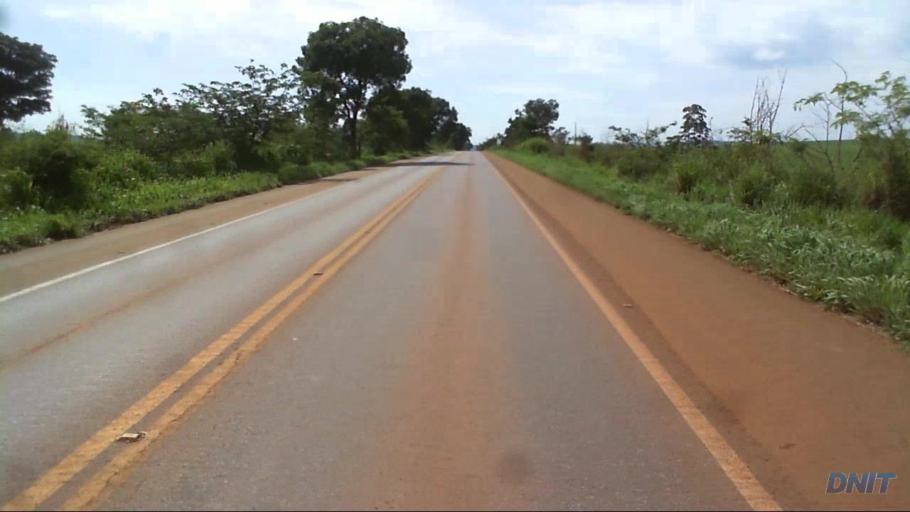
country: BR
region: Goias
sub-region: Barro Alto
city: Barro Alto
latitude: -15.0561
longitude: -48.8805
